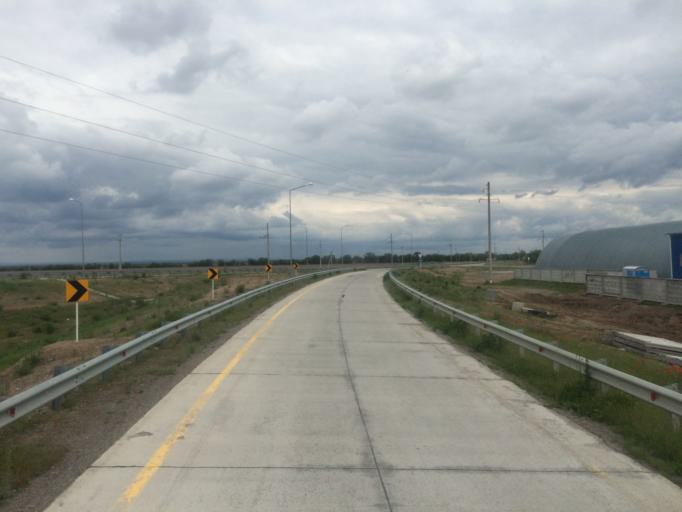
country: KG
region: Chuy
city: Sokuluk
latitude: 43.2733
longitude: 74.2332
